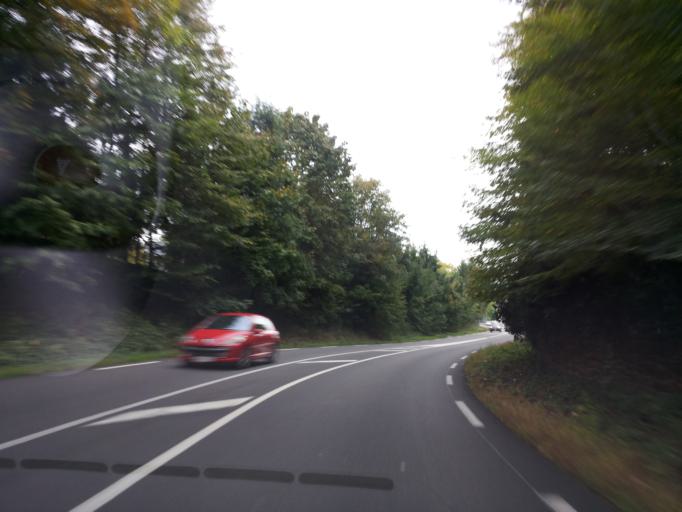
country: FR
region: Alsace
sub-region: Departement du Bas-Rhin
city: Saverne
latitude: 48.7475
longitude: 7.3467
